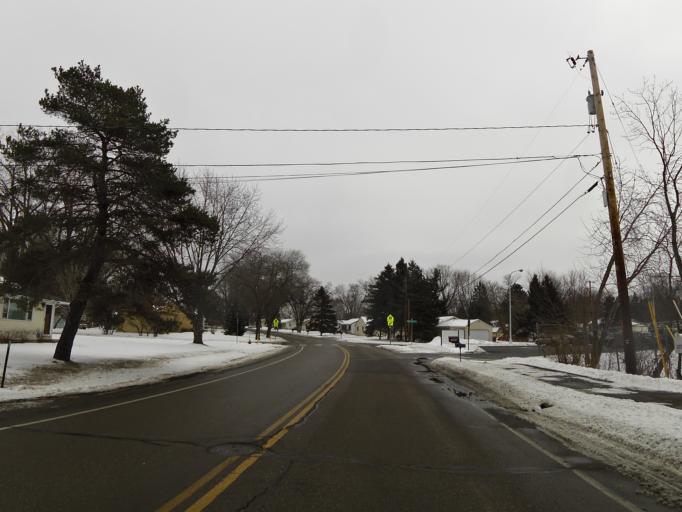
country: US
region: Minnesota
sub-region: Ramsey County
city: North Saint Paul
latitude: 45.0067
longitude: -93.0416
